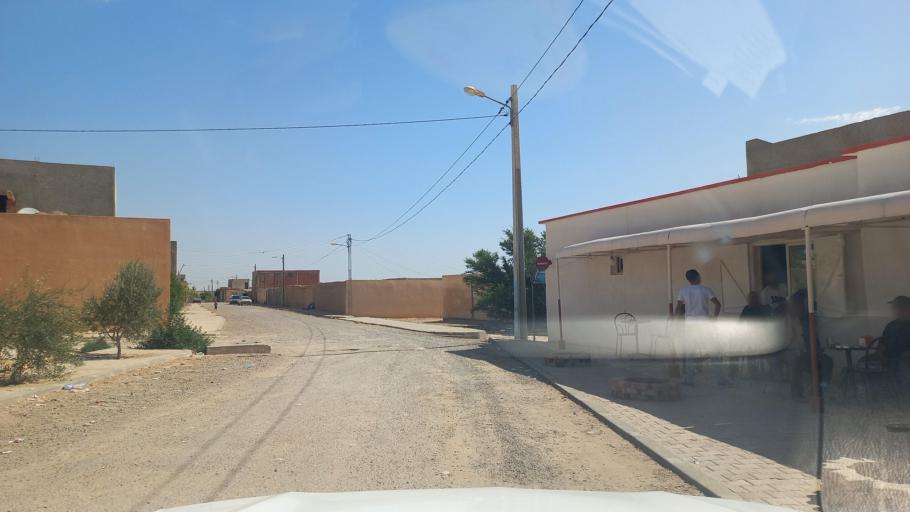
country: TN
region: Al Qasrayn
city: Sbiba
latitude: 35.4447
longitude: 9.0782
